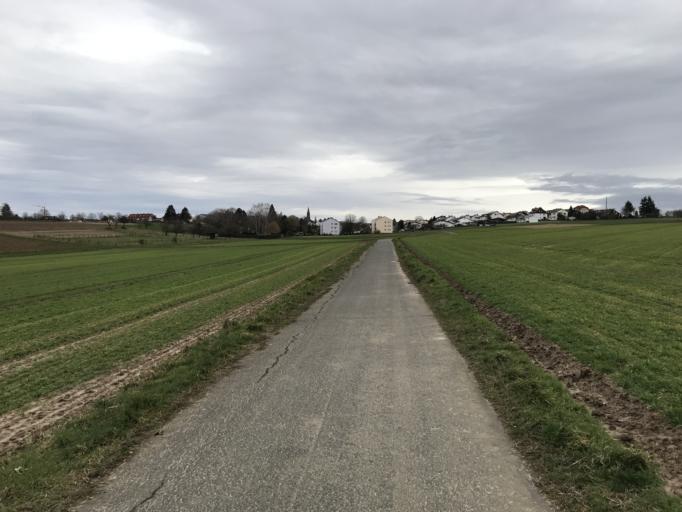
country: DE
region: Hesse
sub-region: Regierungsbezirk Giessen
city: Heuchelheim
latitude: 50.5916
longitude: 8.6236
